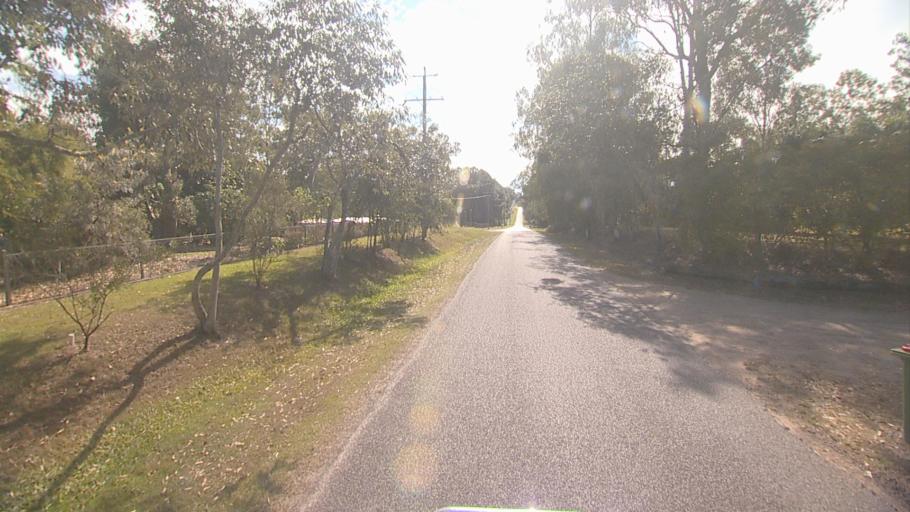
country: AU
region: Queensland
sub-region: Logan
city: North Maclean
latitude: -27.7779
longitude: 152.9909
